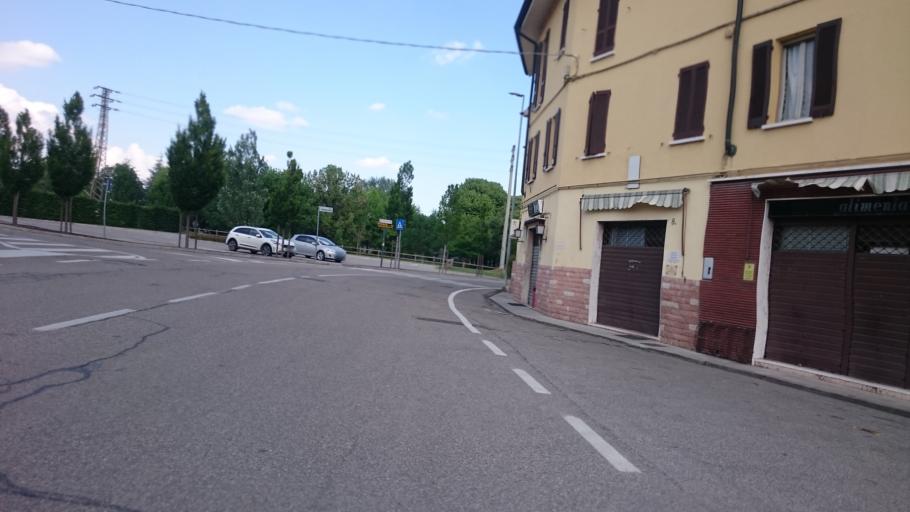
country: IT
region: Lombardy
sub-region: Provincia di Mantova
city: Lunetta-Frassino
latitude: 45.1552
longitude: 10.8235
